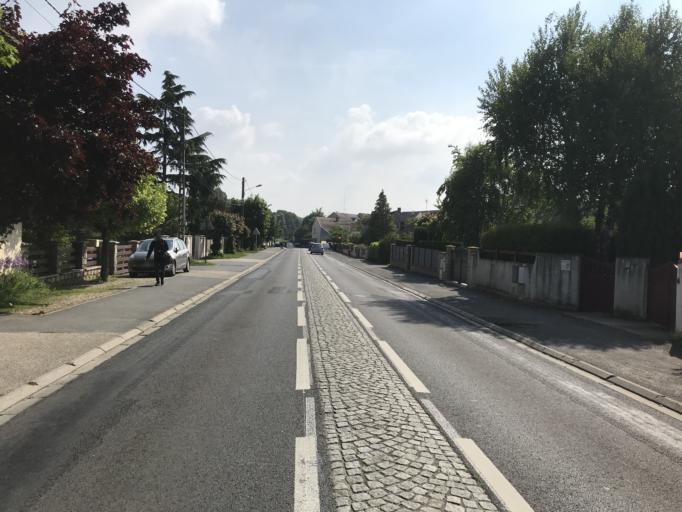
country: FR
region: Ile-de-France
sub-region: Departement de Seine-et-Marne
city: Esbly
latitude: 48.8976
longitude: 2.8069
